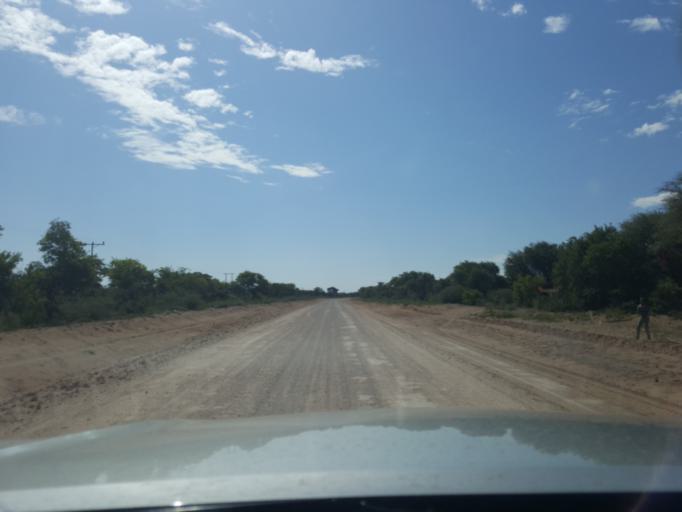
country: BW
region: Kweneng
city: Khudumelapye
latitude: -23.7937
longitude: 24.7925
